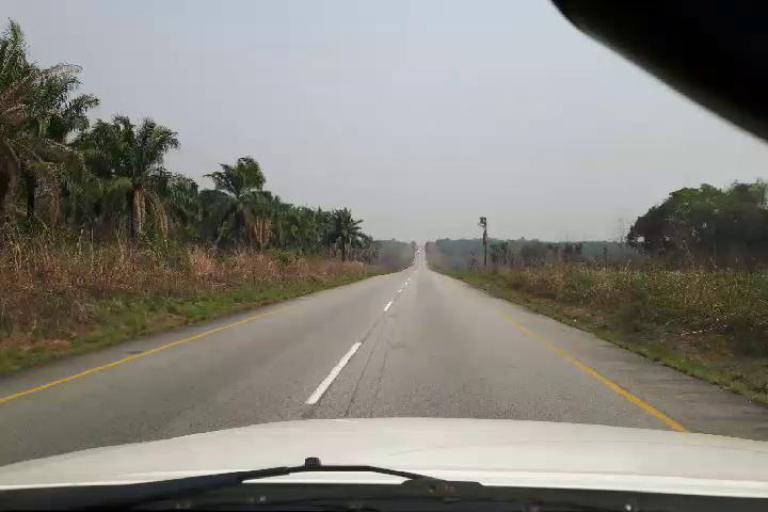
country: SL
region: Southern Province
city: Largo
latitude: 8.2359
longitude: -12.0824
